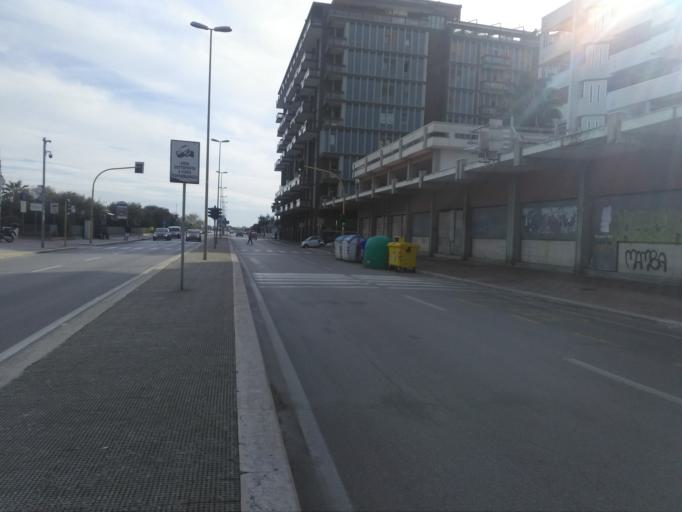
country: IT
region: Apulia
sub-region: Provincia di Bari
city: Bari
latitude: 41.1176
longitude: 16.8918
